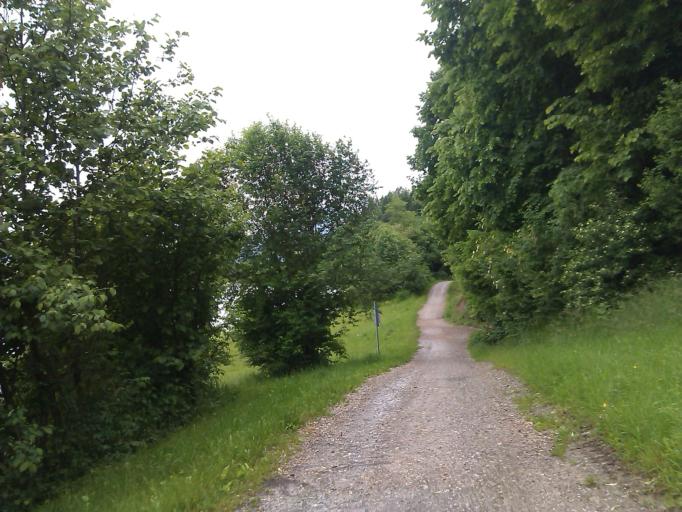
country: DE
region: Bavaria
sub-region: Swabia
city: Schwangau
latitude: 47.6078
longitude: 10.7169
